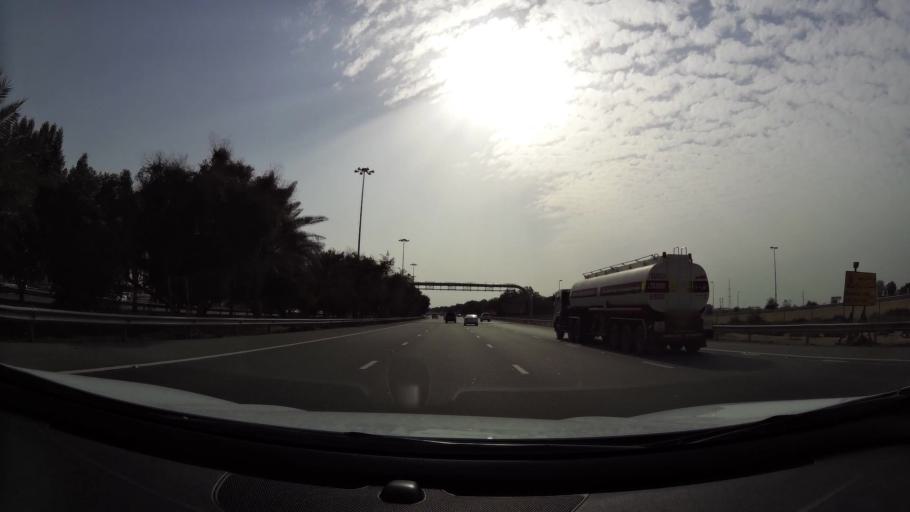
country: AE
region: Abu Dhabi
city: Abu Dhabi
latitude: 24.3189
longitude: 54.6103
